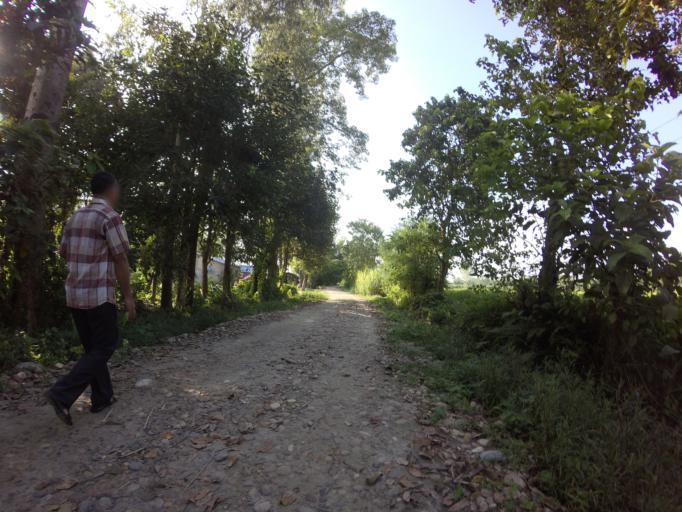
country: NP
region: Far Western
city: Tikapur
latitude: 28.4416
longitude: 81.0769
